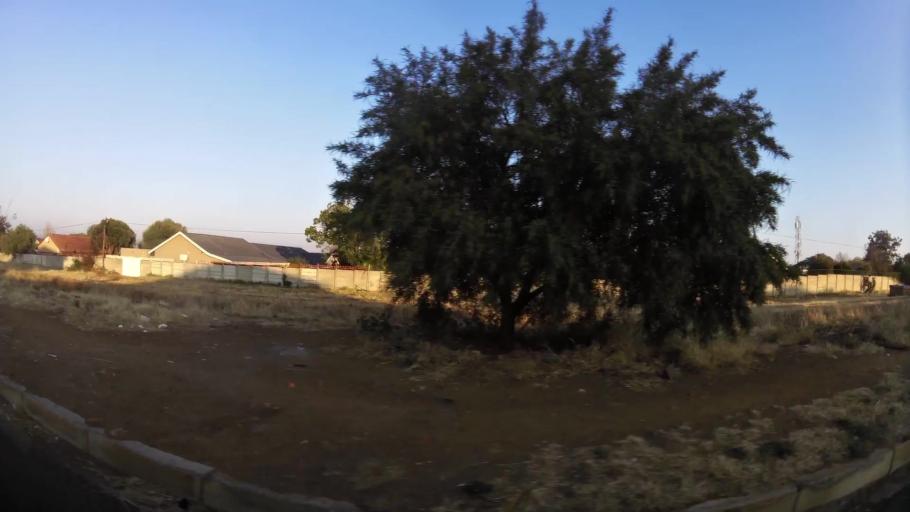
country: ZA
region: Orange Free State
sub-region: Mangaung Metropolitan Municipality
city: Bloemfontein
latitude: -29.0963
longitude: 26.1641
